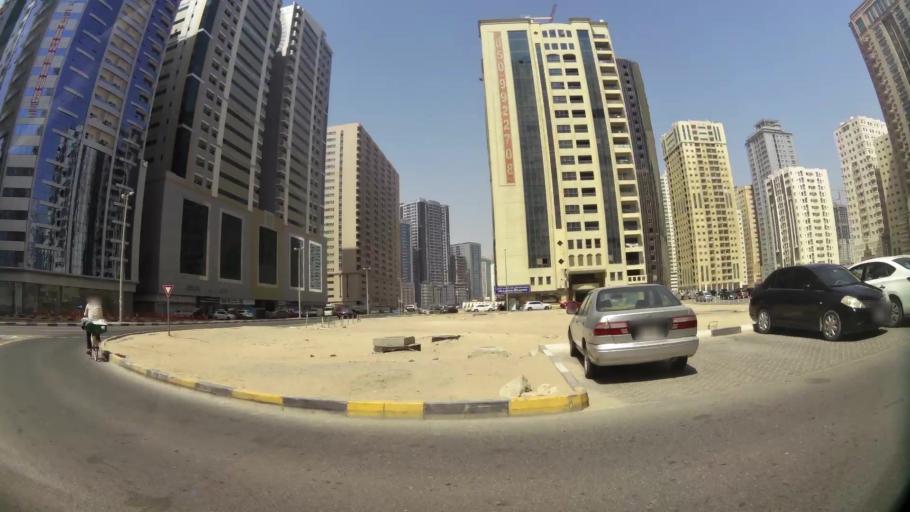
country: AE
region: Ash Shariqah
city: Sharjah
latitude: 25.3012
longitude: 55.3718
